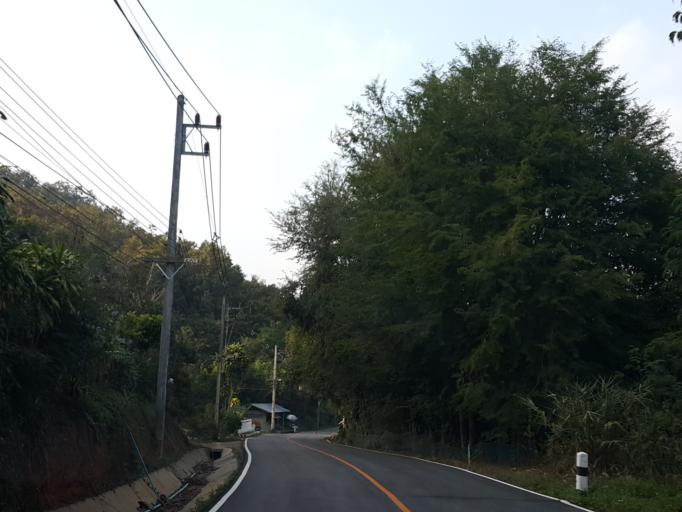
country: TH
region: Chiang Mai
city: Mae On
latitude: 18.8854
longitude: 99.2648
